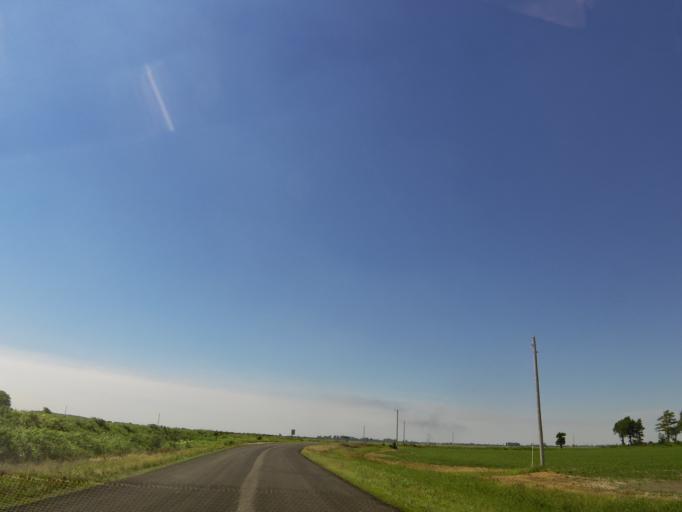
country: US
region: Missouri
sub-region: New Madrid County
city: Lilbourn
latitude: 36.5568
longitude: -89.7030
